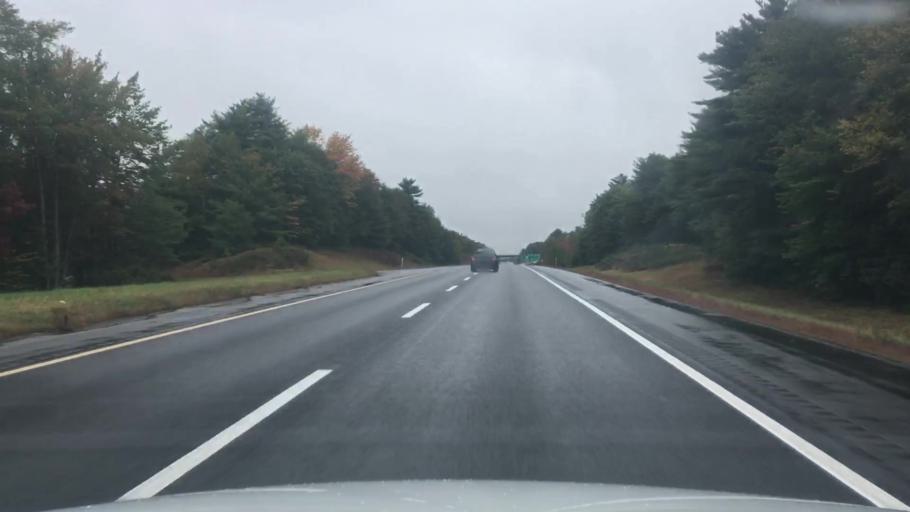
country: US
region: Maine
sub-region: Kennebec County
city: Gardiner
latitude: 44.1696
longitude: -69.8340
